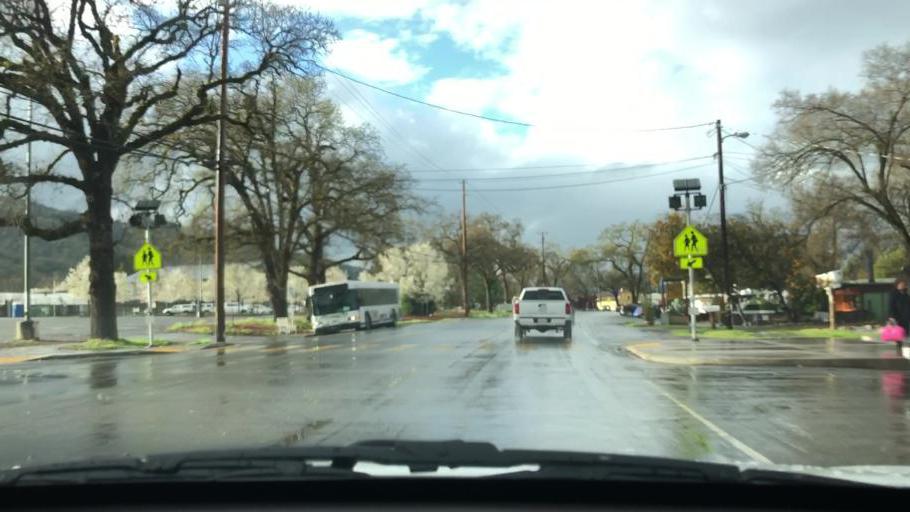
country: US
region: California
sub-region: Mendocino County
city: Ukiah
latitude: 39.1220
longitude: -123.2036
